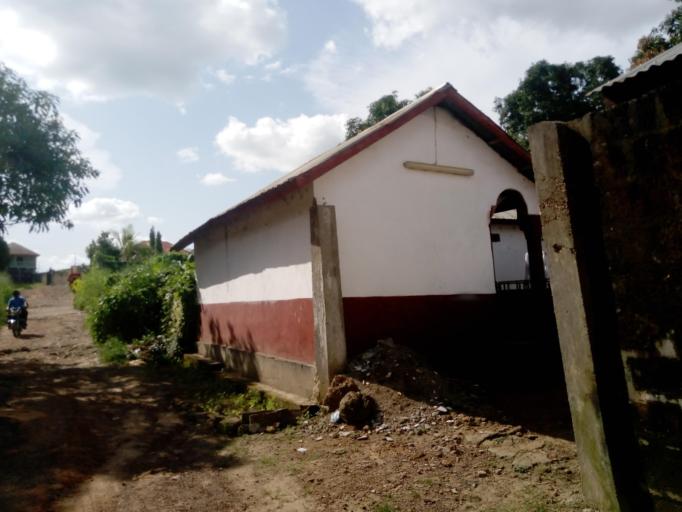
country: SL
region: Northern Province
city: Makeni
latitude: 8.9090
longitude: -12.0327
